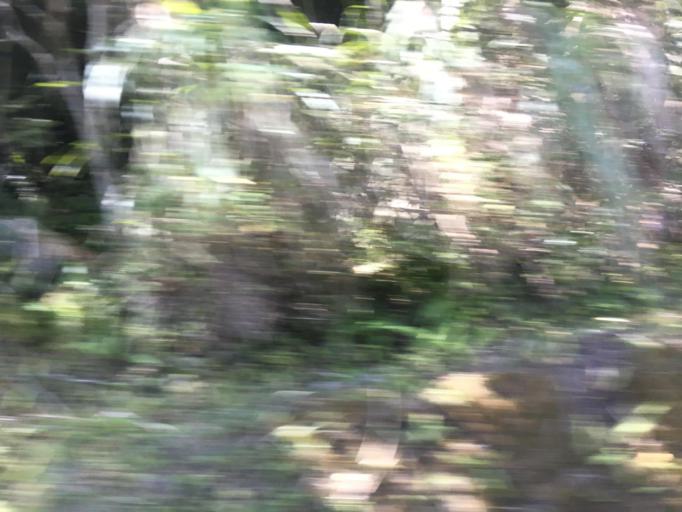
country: TW
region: Taiwan
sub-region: Yilan
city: Yilan
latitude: 24.5404
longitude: 121.5131
